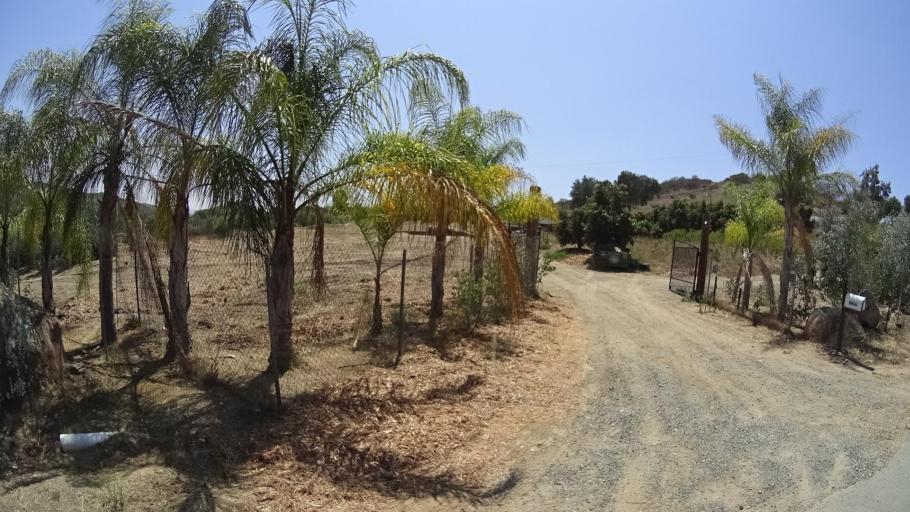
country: US
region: California
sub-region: San Diego County
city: Fallbrook
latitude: 33.4124
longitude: -117.2817
